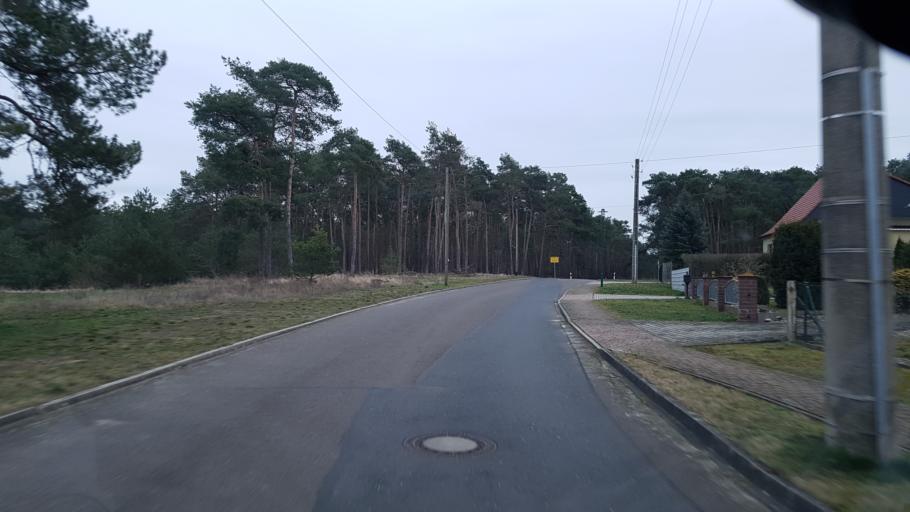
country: DE
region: Brandenburg
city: Schlieben
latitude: 51.7106
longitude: 13.3078
